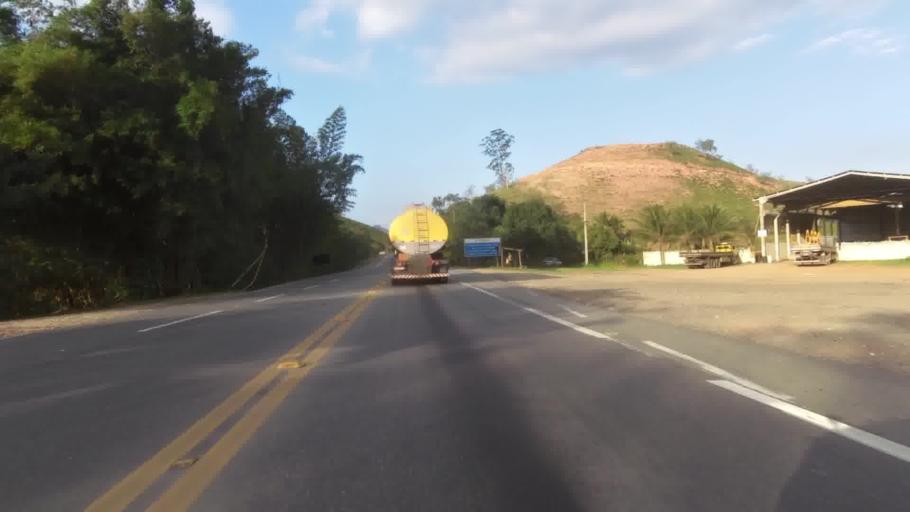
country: BR
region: Espirito Santo
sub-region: Rio Novo Do Sul
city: Rio Novo do Sul
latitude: -20.8825
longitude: -40.9783
